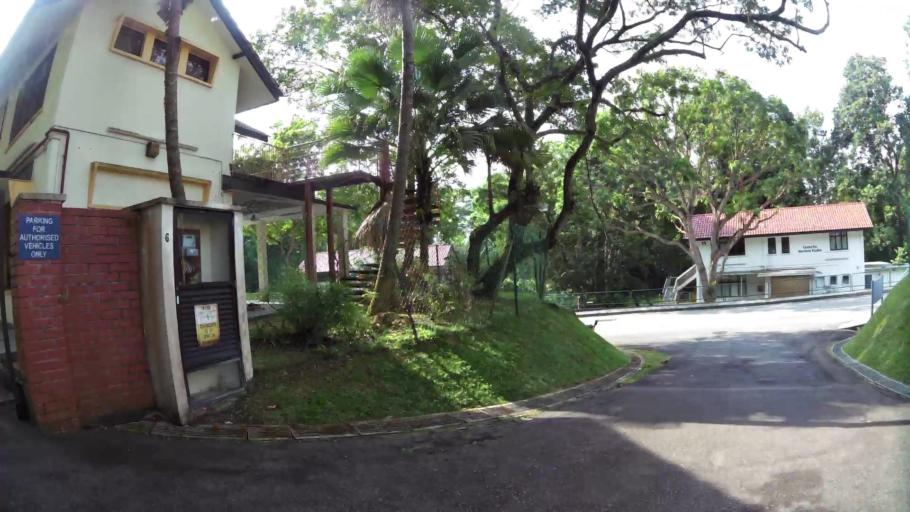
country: SG
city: Singapore
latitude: 1.2932
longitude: 103.7782
